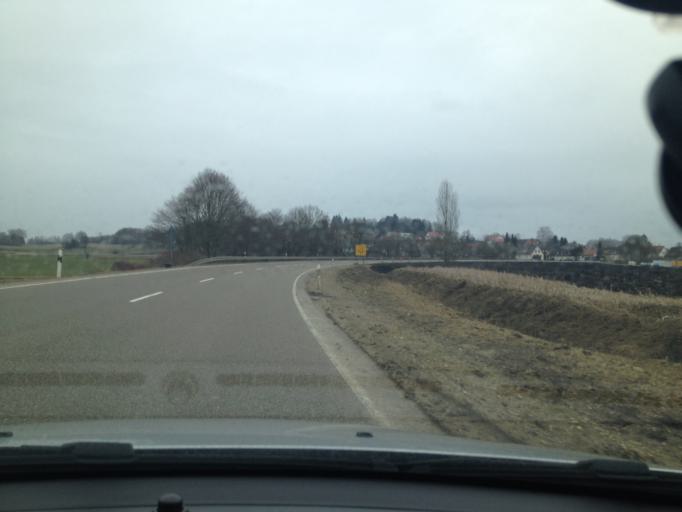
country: DE
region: Bavaria
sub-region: Swabia
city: Rofingen
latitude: 48.4275
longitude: 10.4355
